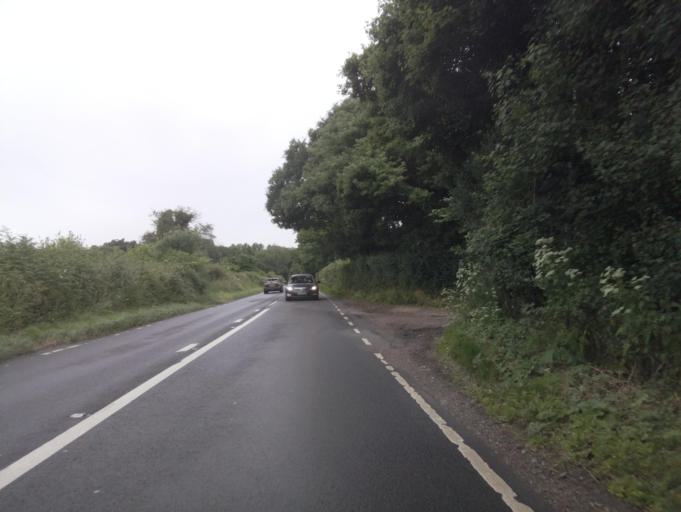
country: GB
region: England
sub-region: Devon
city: Axminster
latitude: 50.8015
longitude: -2.9807
